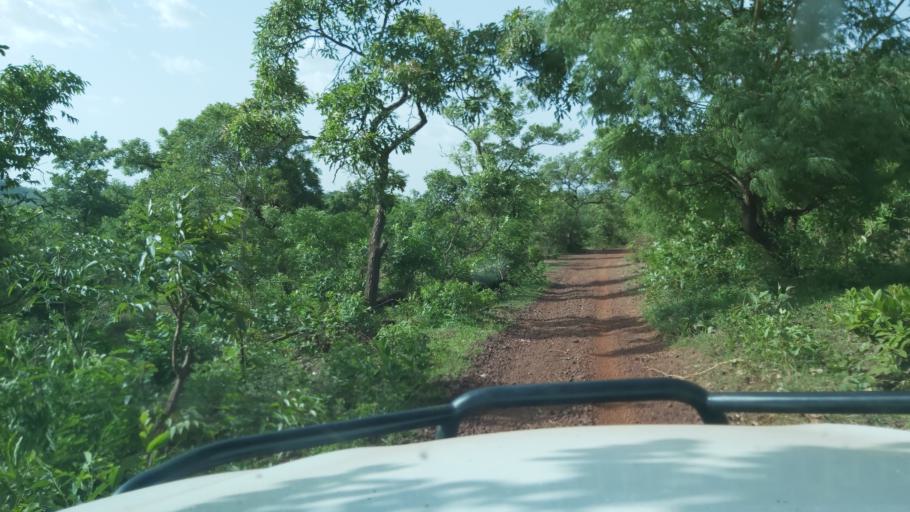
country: ML
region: Koulikoro
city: Kangaba
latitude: 12.4024
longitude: -8.8866
